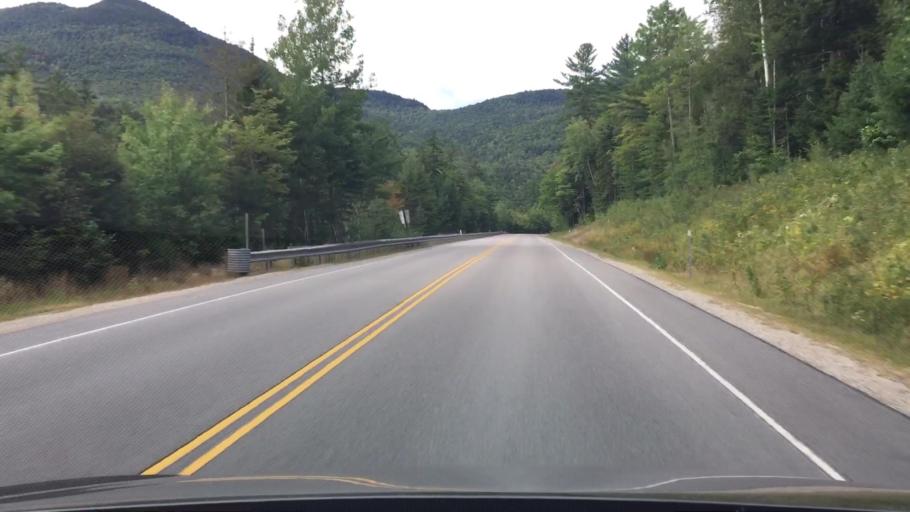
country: US
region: New Hampshire
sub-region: Carroll County
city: Tamworth
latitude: 44.0027
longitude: -71.2771
